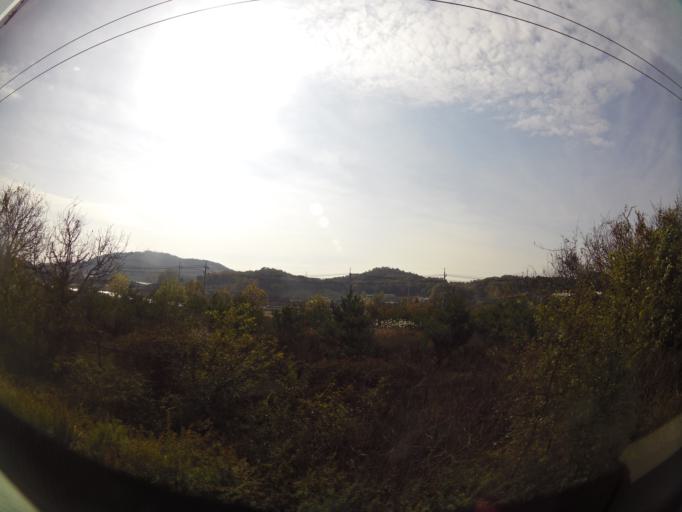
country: KR
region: Daejeon
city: Songgang-dong
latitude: 36.5375
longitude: 127.3441
